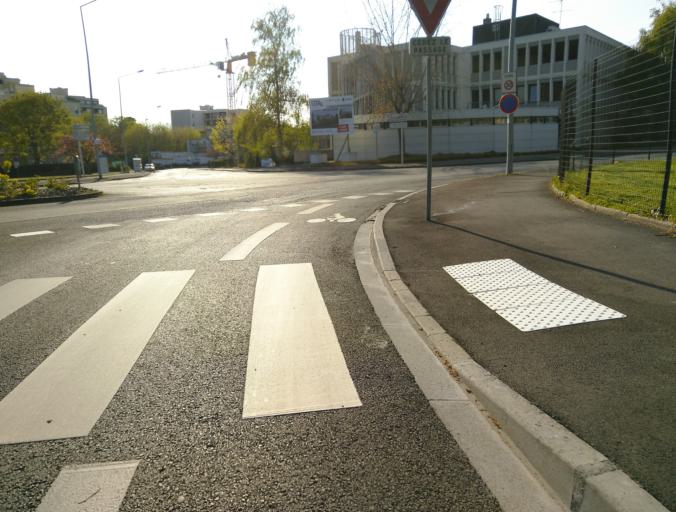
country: FR
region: Pays de la Loire
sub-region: Departement de Maine-et-Loire
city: Angers
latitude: 47.4479
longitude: -0.5432
